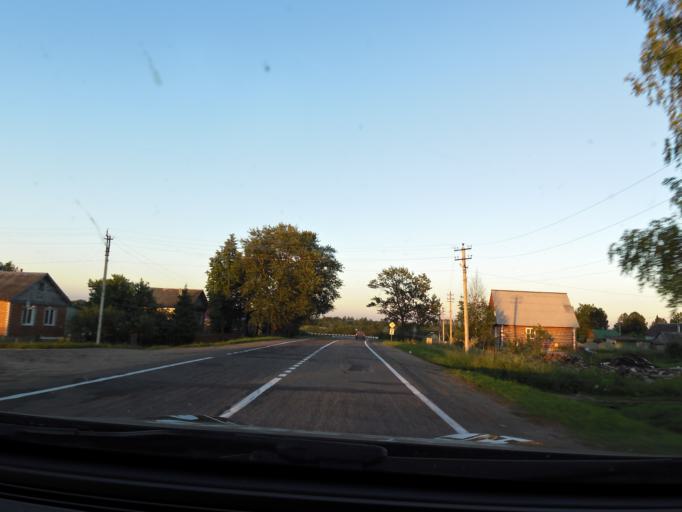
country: RU
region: Jaroslavl
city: Lyubim
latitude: 58.3561
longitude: 40.6556
